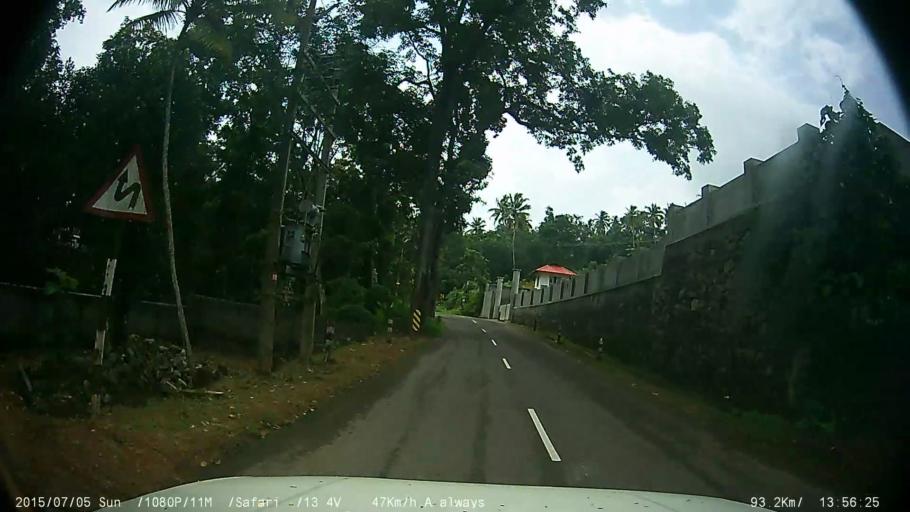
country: IN
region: Kerala
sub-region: Kottayam
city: Palackattumala
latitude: 9.7587
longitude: 76.5828
